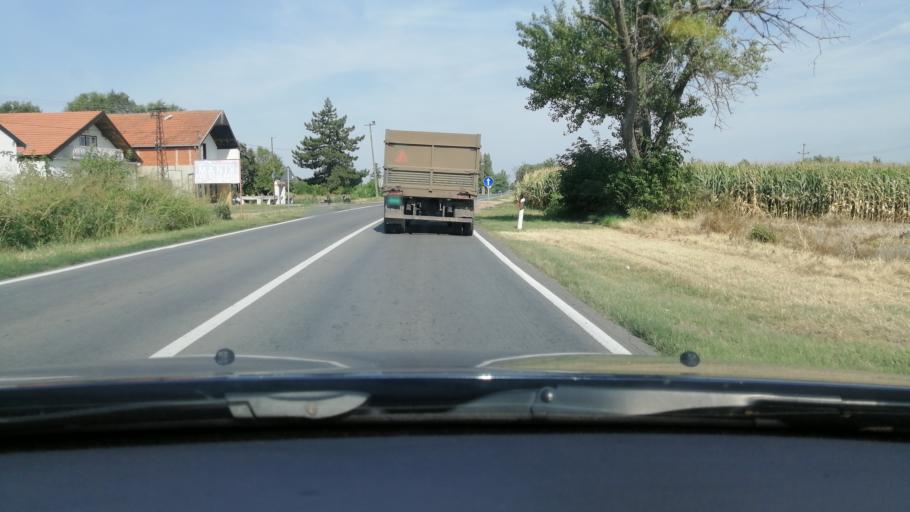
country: RS
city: Ecka
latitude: 45.3321
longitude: 20.4377
